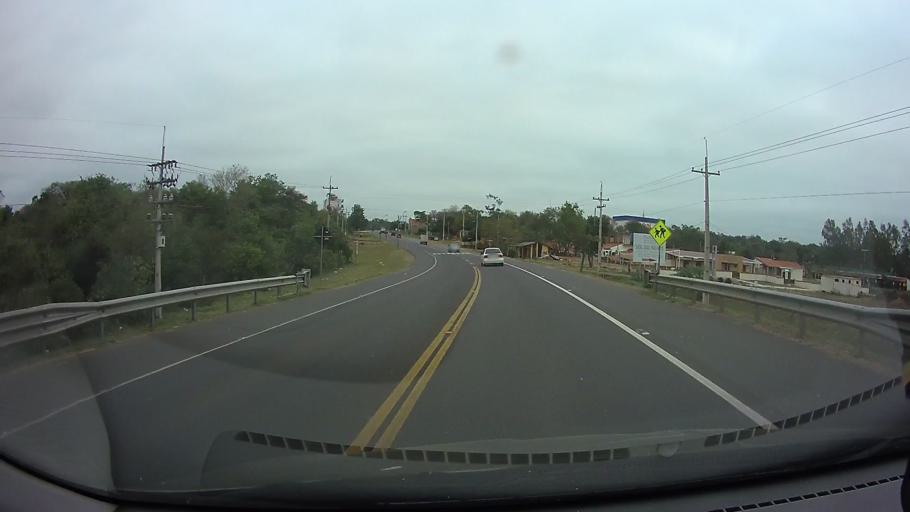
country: PY
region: Central
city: Limpio
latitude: -25.1307
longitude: -57.4463
